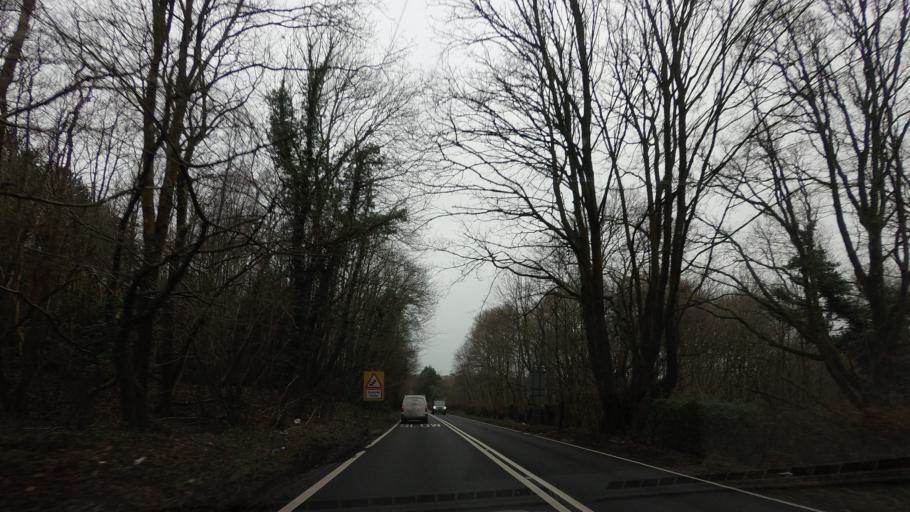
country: GB
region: England
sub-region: East Sussex
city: Saint Leonards-on-Sea
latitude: 50.8997
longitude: 0.5544
